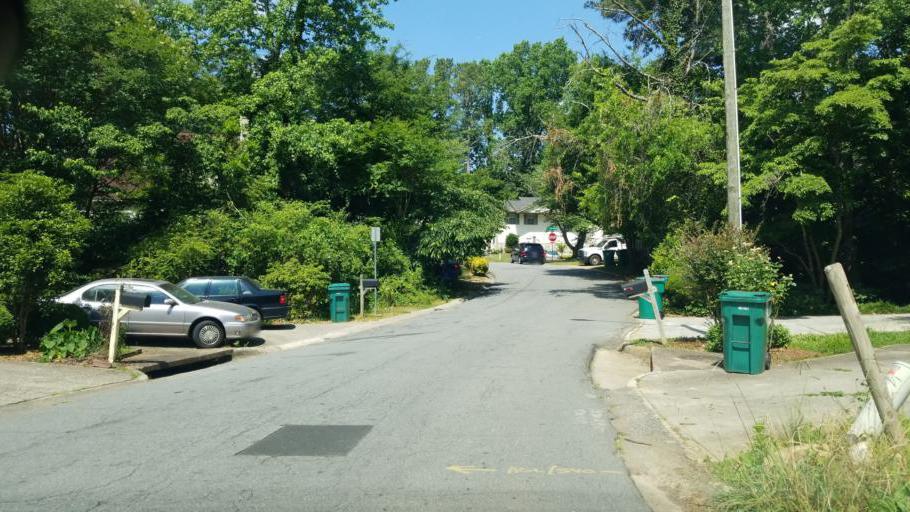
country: US
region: Georgia
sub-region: Cobb County
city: Vinings
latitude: 33.8872
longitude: -84.4833
